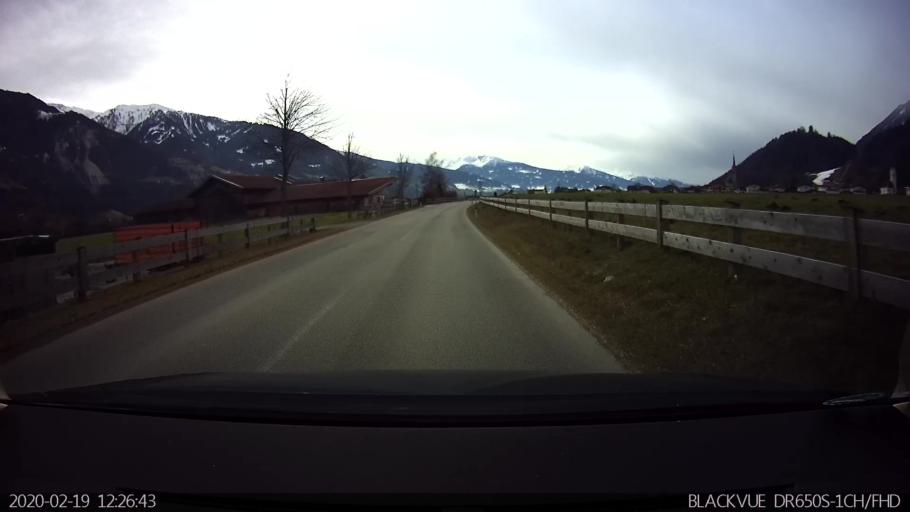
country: AT
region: Tyrol
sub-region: Politischer Bezirk Schwaz
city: Stans
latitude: 47.3729
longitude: 11.7244
